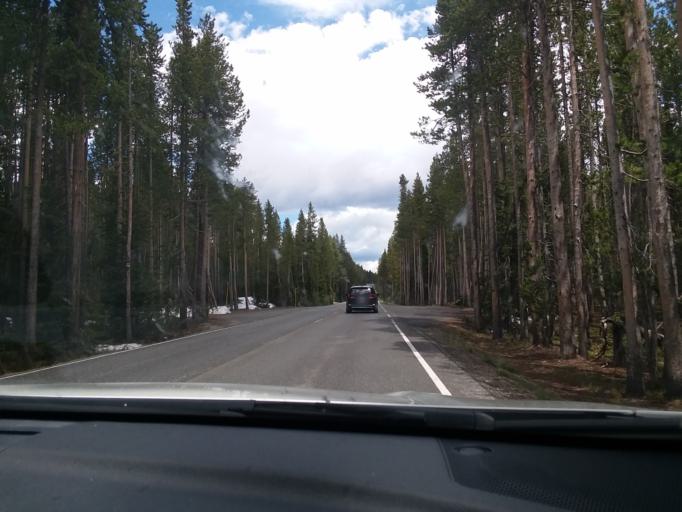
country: US
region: Idaho
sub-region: Teton County
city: Driggs
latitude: 44.1828
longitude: -110.6590
